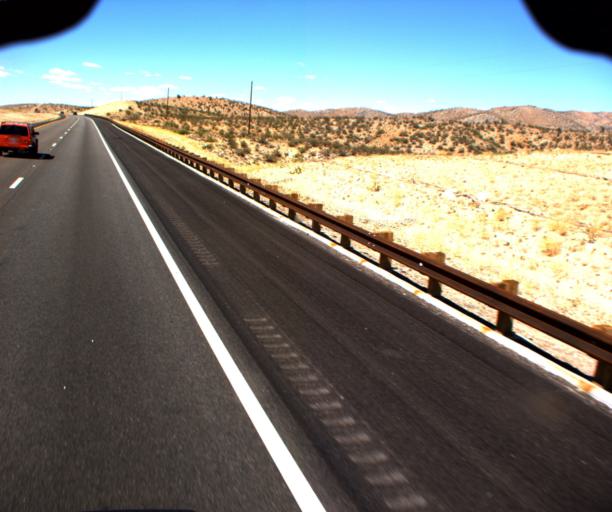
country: US
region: Arizona
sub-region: Mohave County
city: Kingman
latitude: 34.9932
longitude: -113.6650
